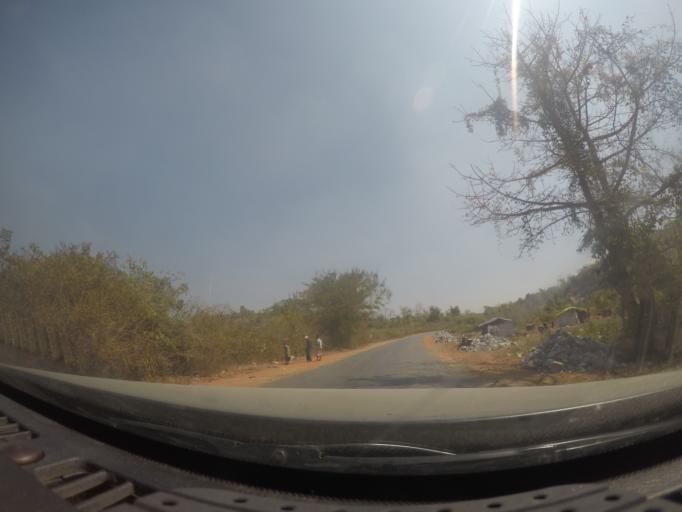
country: MM
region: Shan
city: Taunggyi
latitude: 20.8113
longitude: 97.2366
